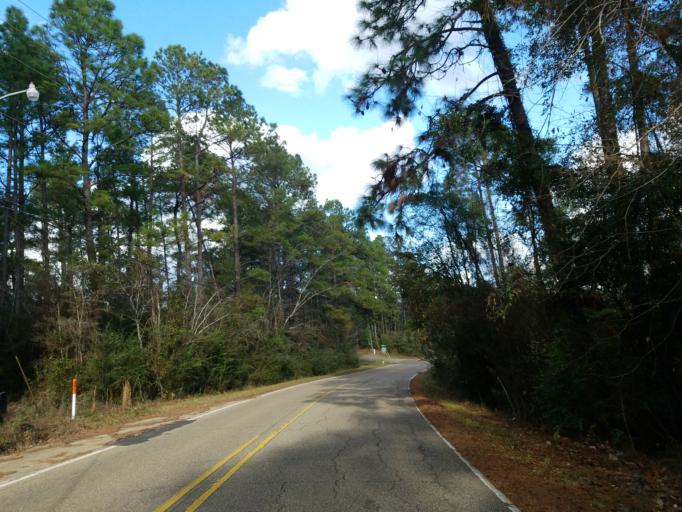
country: US
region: Mississippi
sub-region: Lamar County
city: West Hattiesburg
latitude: 31.2889
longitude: -89.3328
